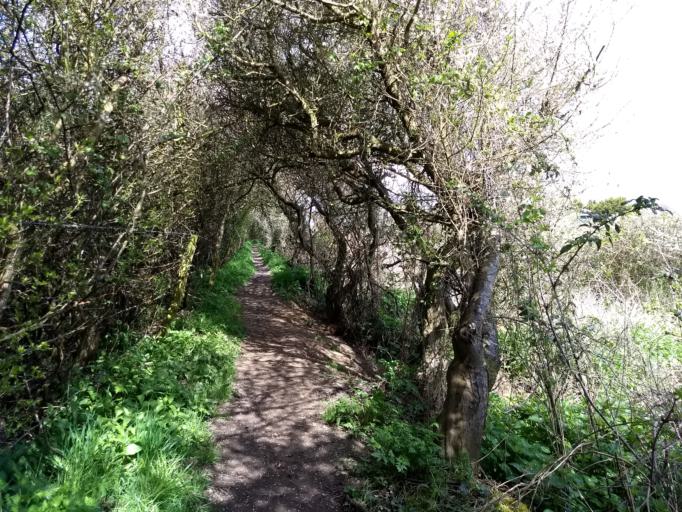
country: GB
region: England
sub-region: Isle of Wight
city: East Cowes
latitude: 50.7339
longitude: -1.2309
